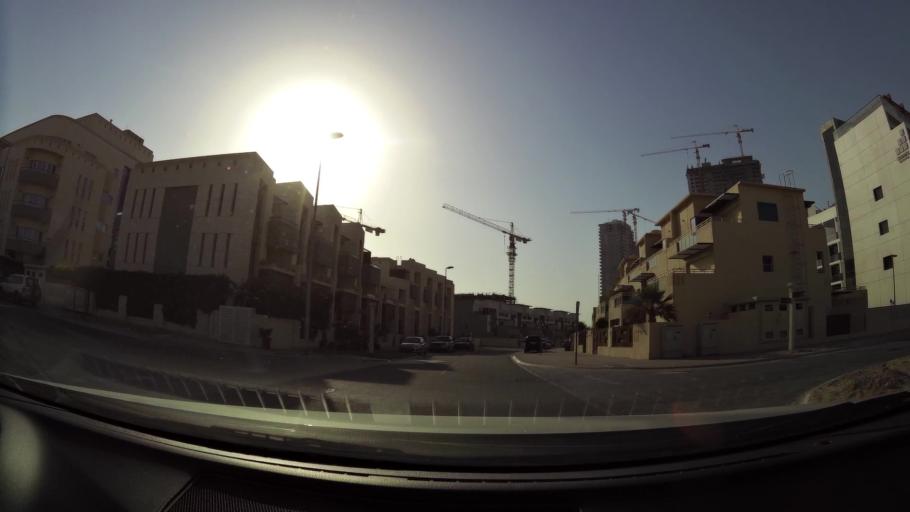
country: AE
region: Dubai
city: Dubai
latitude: 25.0498
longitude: 55.2001
